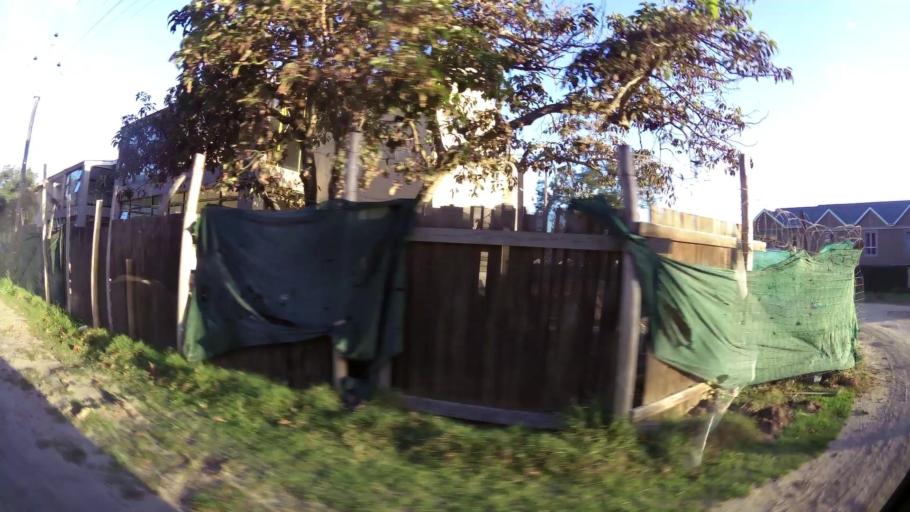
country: ZA
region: Western Cape
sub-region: Eden District Municipality
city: Knysna
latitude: -34.0114
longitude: 22.7976
